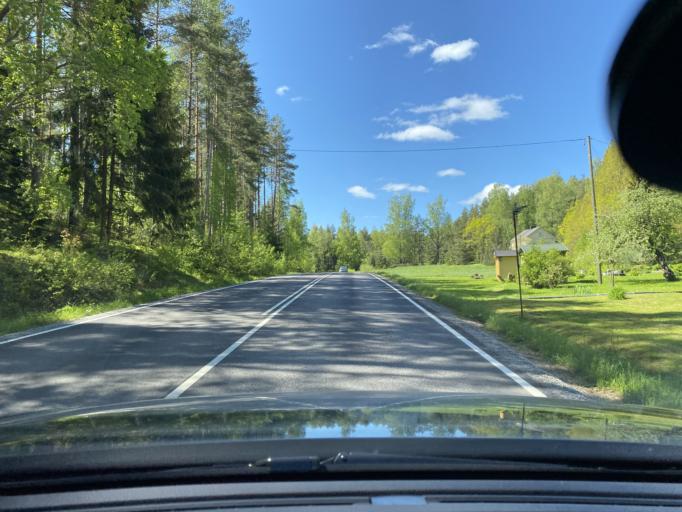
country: FI
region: Varsinais-Suomi
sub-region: Salo
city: Halikko
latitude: 60.3629
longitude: 22.9888
